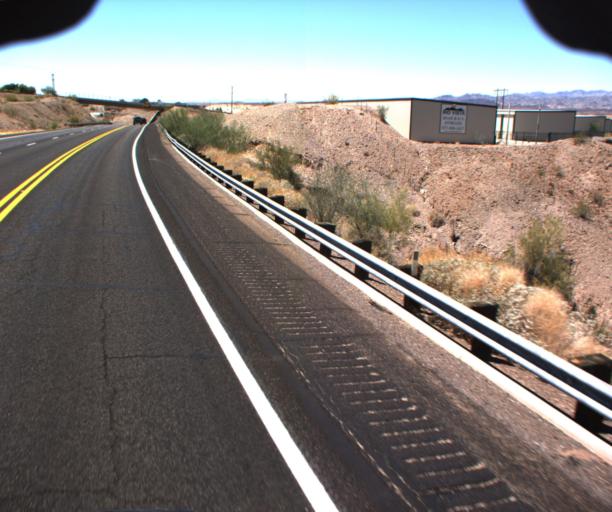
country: US
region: Arizona
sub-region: La Paz County
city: Cienega Springs
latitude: 34.1847
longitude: -114.2193
